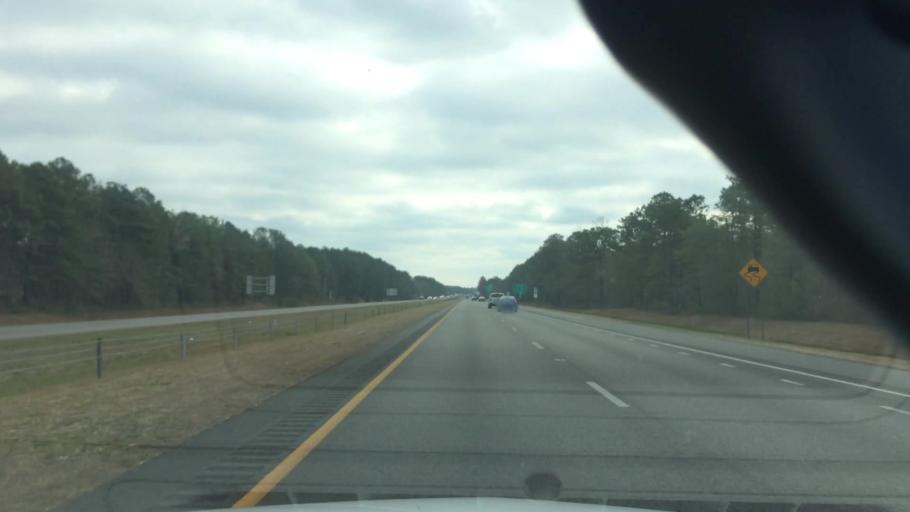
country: US
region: North Carolina
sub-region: New Hanover County
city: Castle Hayne
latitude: 34.3459
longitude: -77.8817
